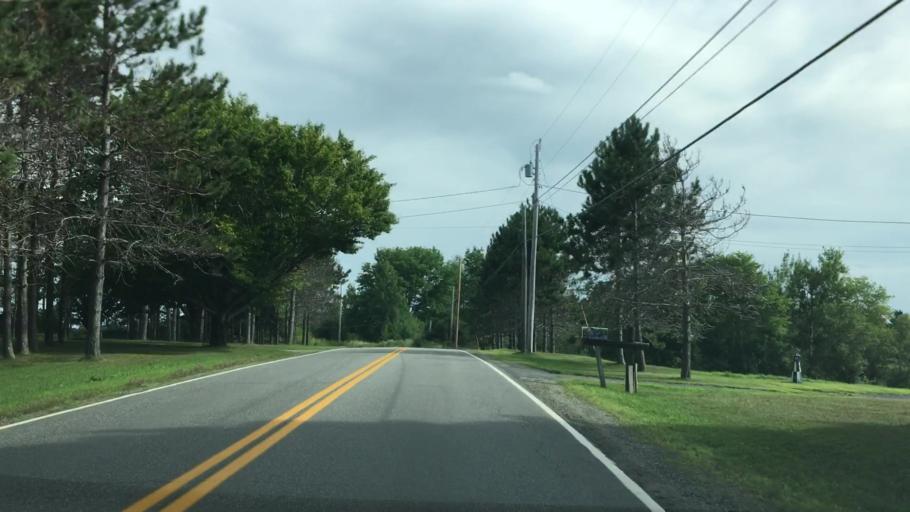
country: US
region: Maine
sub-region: Waldo County
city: Belfast
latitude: 44.3792
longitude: -69.0342
